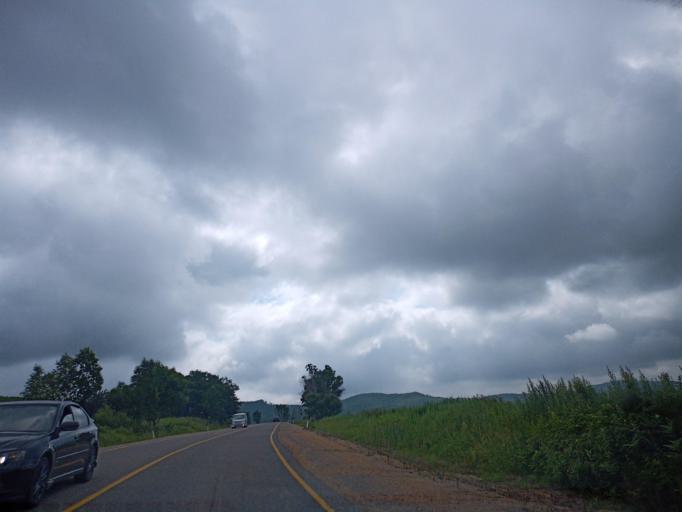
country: RU
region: Primorskiy
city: Dal'nerechensk
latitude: 46.0384
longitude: 133.8831
